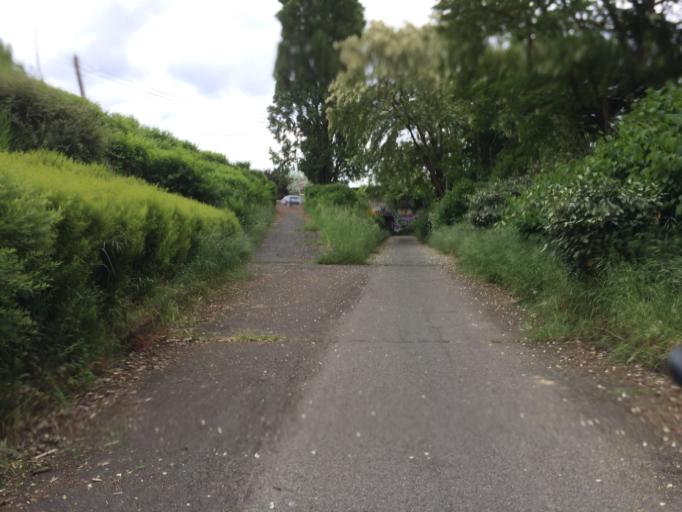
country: FR
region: Ile-de-France
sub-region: Departement de l'Essonne
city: Saulx-les-Chartreux
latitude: 48.6829
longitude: 2.2836
